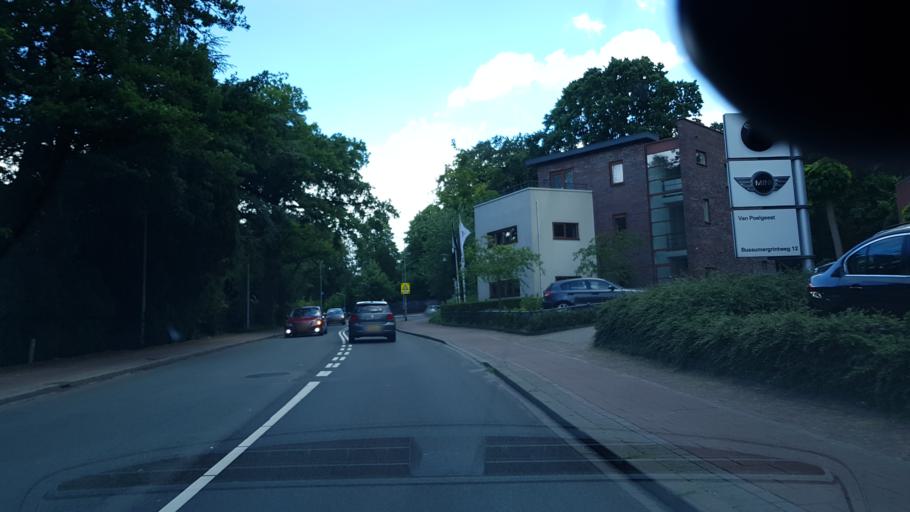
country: NL
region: North Holland
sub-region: Gemeente Hilversum
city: Hilversum
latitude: 52.2334
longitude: 5.1596
